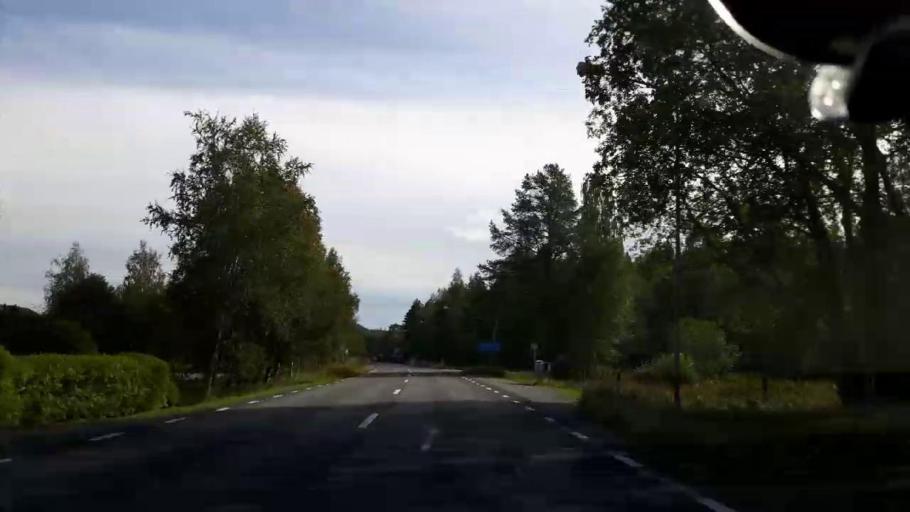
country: SE
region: Jaemtland
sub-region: Braecke Kommun
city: Braecke
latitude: 63.1636
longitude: 15.5658
